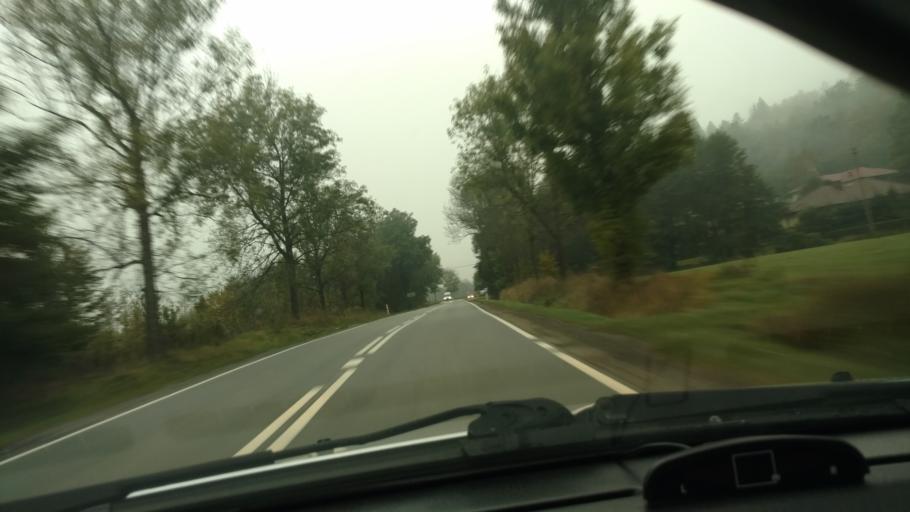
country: PL
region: Subcarpathian Voivodeship
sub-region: Powiat strzyzowski
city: Frysztak
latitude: 49.8576
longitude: 21.6234
